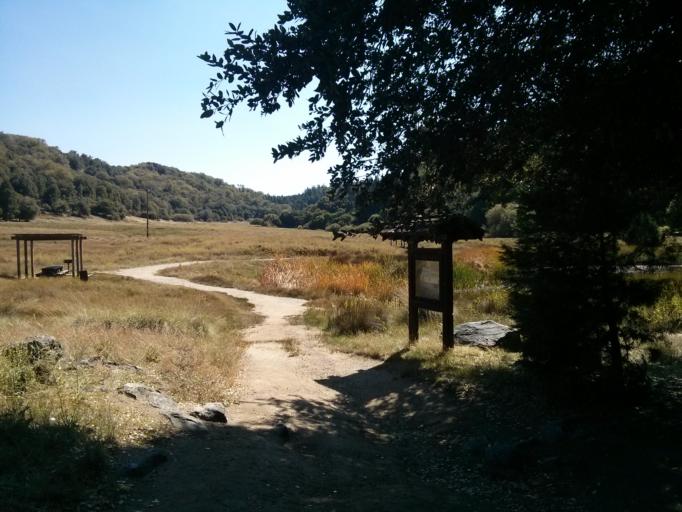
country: US
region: California
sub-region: Riverside County
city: Aguanga
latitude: 33.3408
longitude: -116.9014
